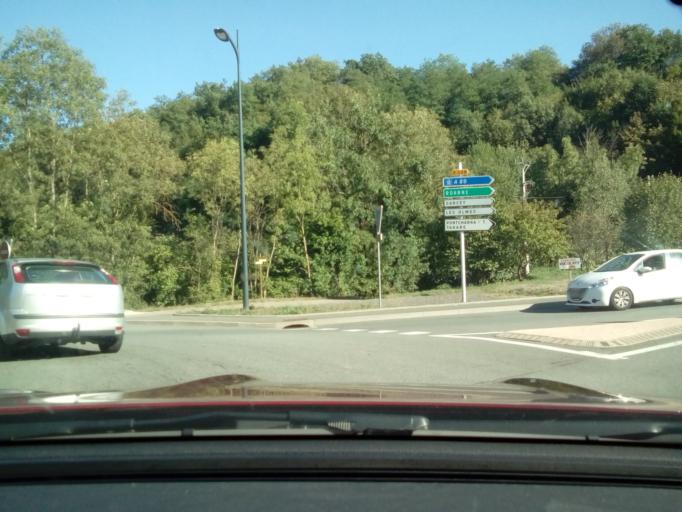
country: FR
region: Rhone-Alpes
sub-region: Departement du Rhone
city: Saint-Verand
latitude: 45.9055
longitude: 4.5730
